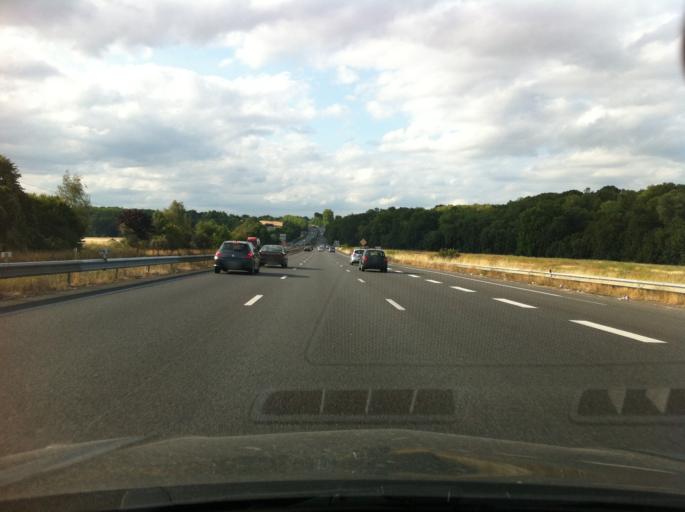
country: FR
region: Ile-de-France
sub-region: Departement de Seine-et-Marne
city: Brie-Comte-Robert
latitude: 48.6658
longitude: 2.6131
